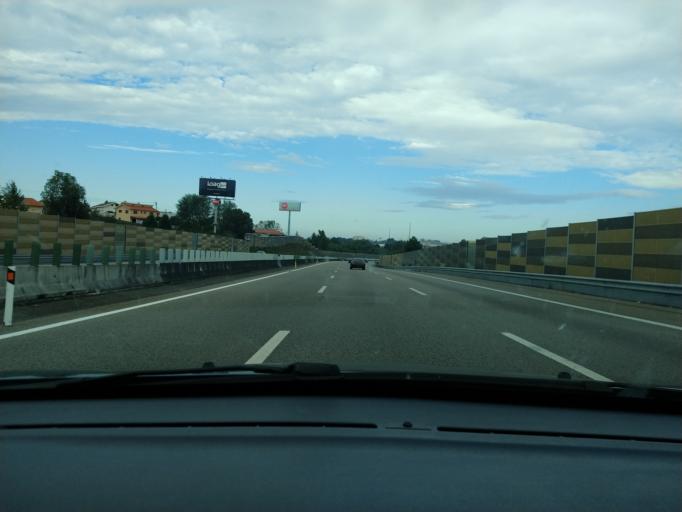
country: PT
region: Aveiro
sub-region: Santa Maria da Feira
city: Pacos de Brandao
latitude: 40.9734
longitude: -8.5734
